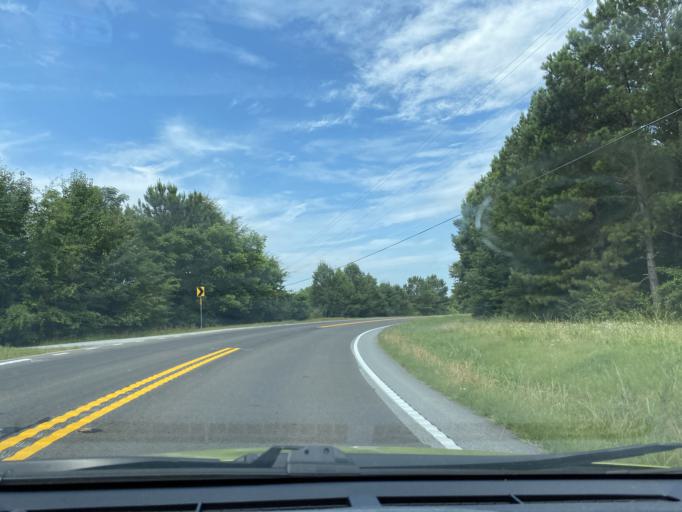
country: US
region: Georgia
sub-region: Coweta County
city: Senoia
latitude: 33.3038
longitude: -84.6563
